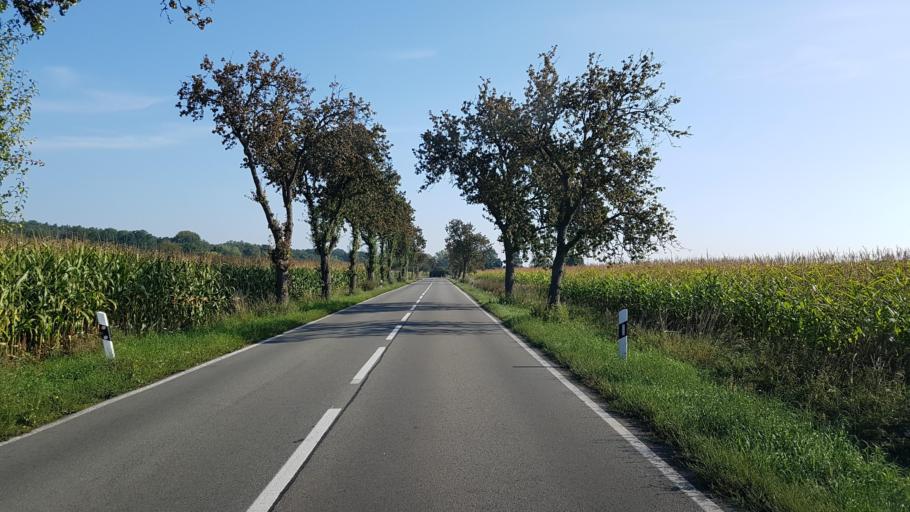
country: DE
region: Brandenburg
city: Brandenburg an der Havel
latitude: 52.4810
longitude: 12.5930
